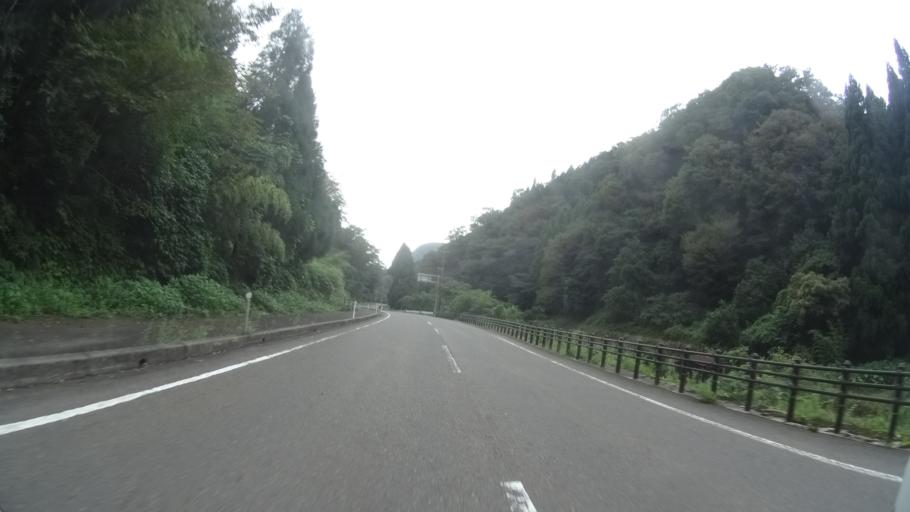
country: JP
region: Tottori
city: Kurayoshi
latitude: 35.4008
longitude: 133.9642
